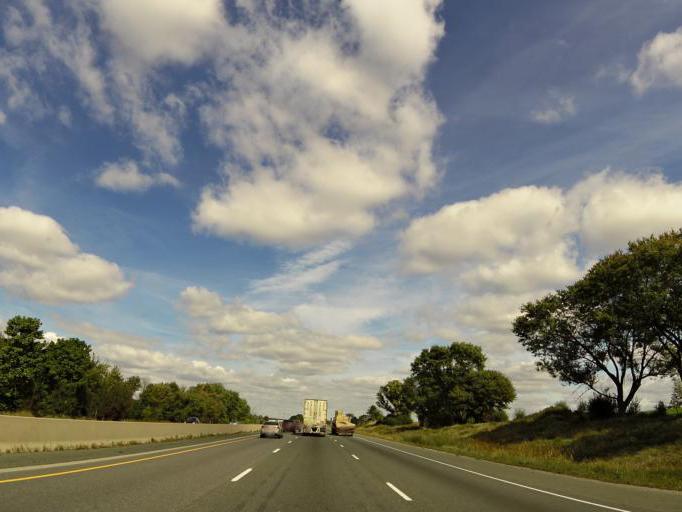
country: CA
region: Ontario
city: Ingersoll
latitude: 42.9986
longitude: -80.8976
